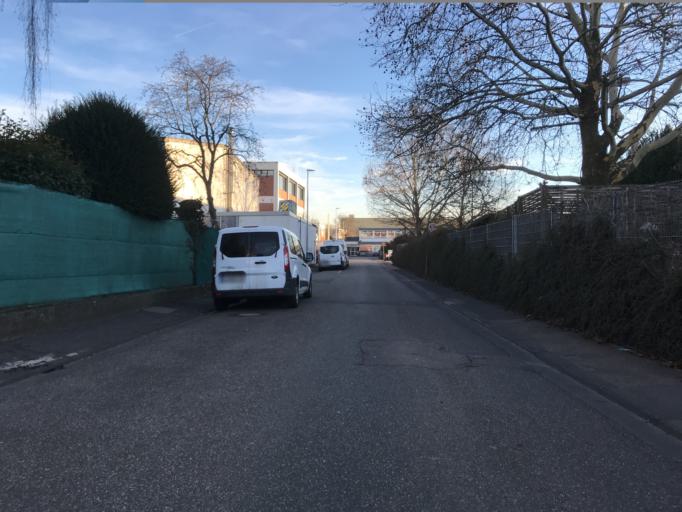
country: DE
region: Rheinland-Pfalz
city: Mainz
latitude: 49.9680
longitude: 8.2665
